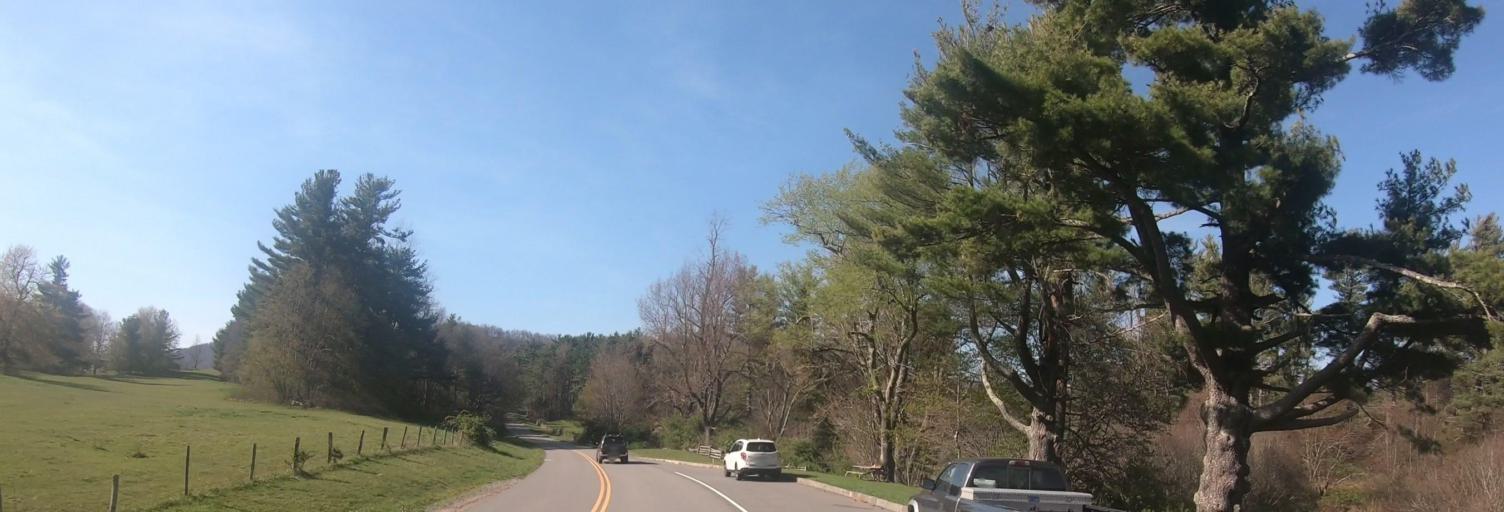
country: US
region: North Carolina
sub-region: Watauga County
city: Boone
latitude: 36.1977
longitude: -81.6044
